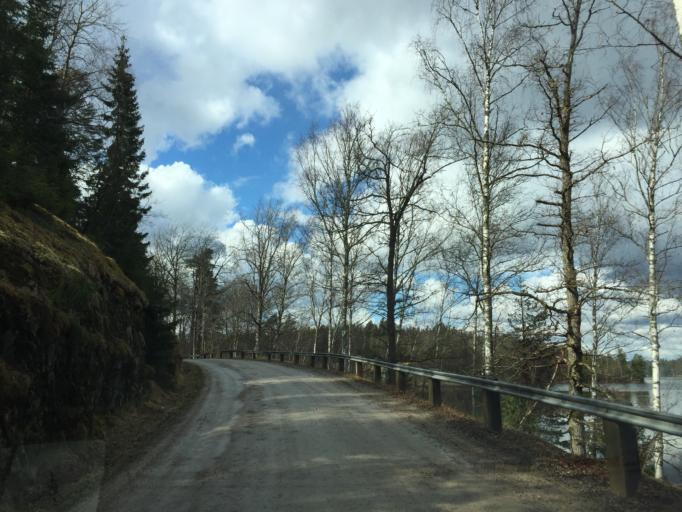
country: SE
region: Soedermanland
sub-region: Nykopings Kommun
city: Nykoping
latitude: 58.9697
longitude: 17.0315
